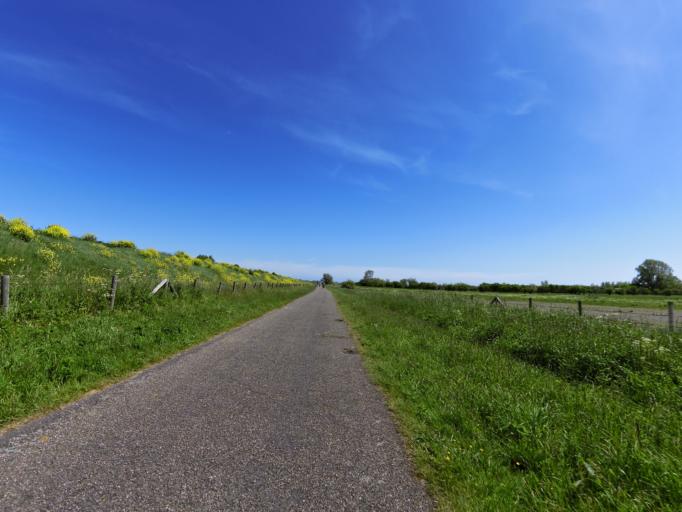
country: NL
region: South Holland
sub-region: Gemeente Hellevoetsluis
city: Nieuw-Helvoet
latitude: 51.8303
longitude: 4.1030
